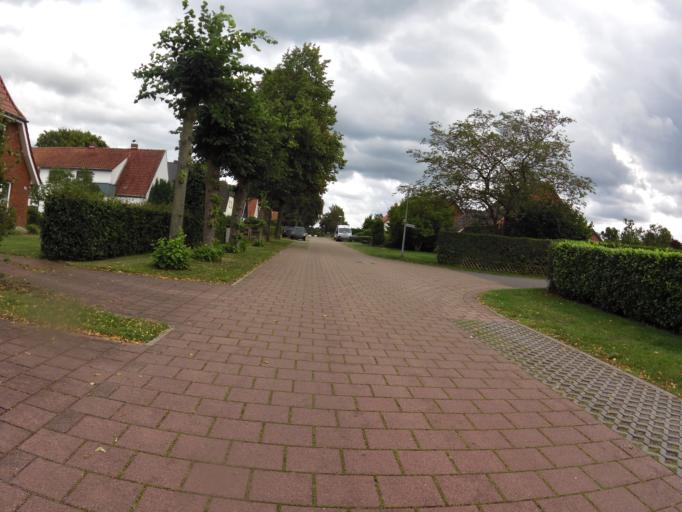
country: DE
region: Lower Saxony
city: Kohlen
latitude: 53.5101
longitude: 8.8647
